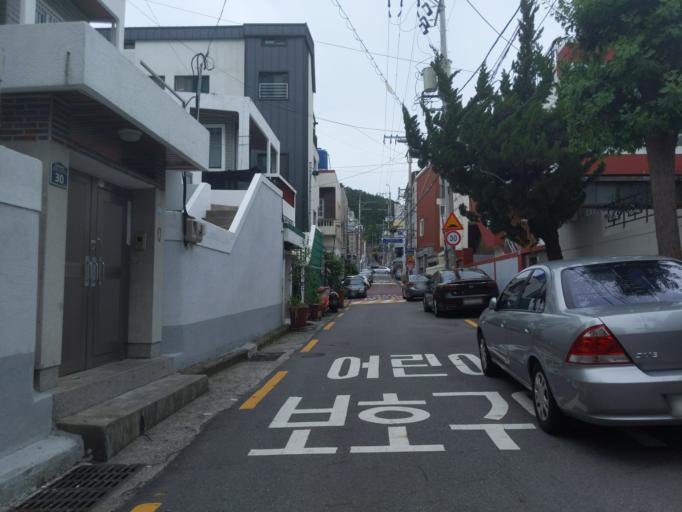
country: KR
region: Busan
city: Busan
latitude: 35.1582
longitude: 129.1276
